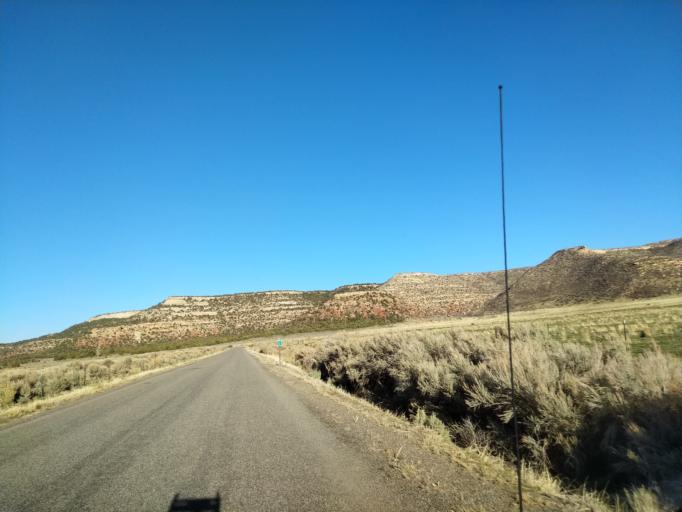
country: US
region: Colorado
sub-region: Mesa County
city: Loma
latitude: 38.9490
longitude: -109.0352
